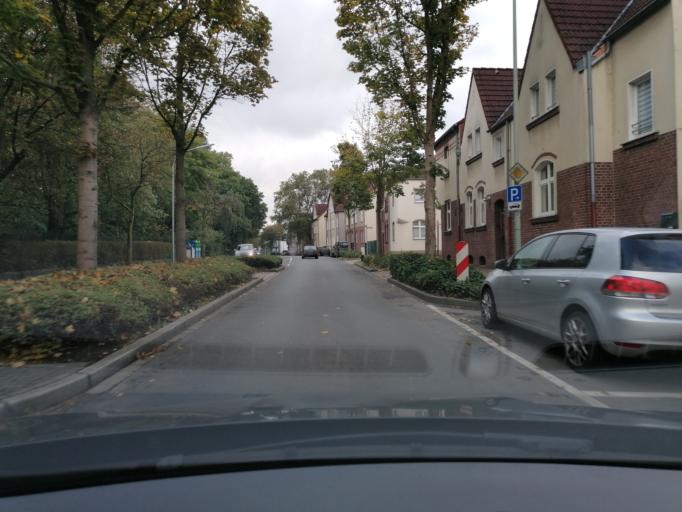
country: DE
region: North Rhine-Westphalia
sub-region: Regierungsbezirk Munster
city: Gelsenkirchen
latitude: 51.5345
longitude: 7.1499
